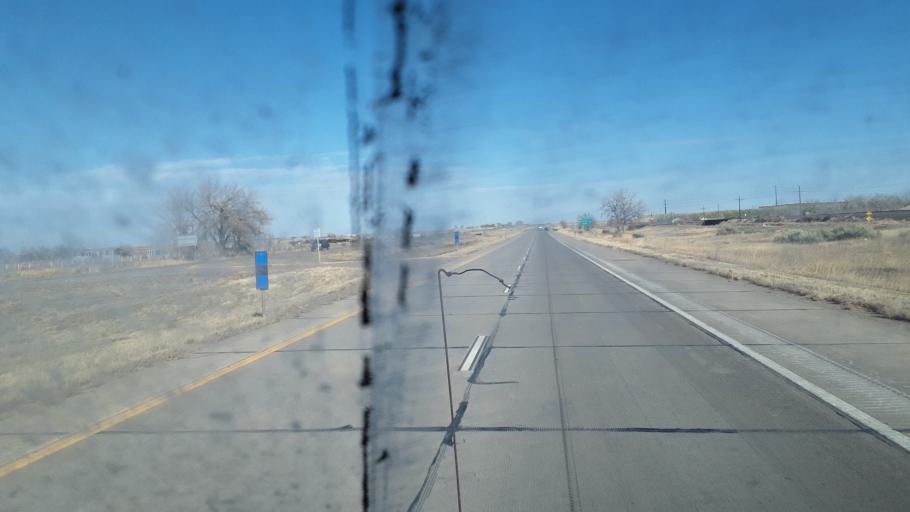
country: US
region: Colorado
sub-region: Weld County
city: Hudson
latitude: 40.0963
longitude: -104.6104
